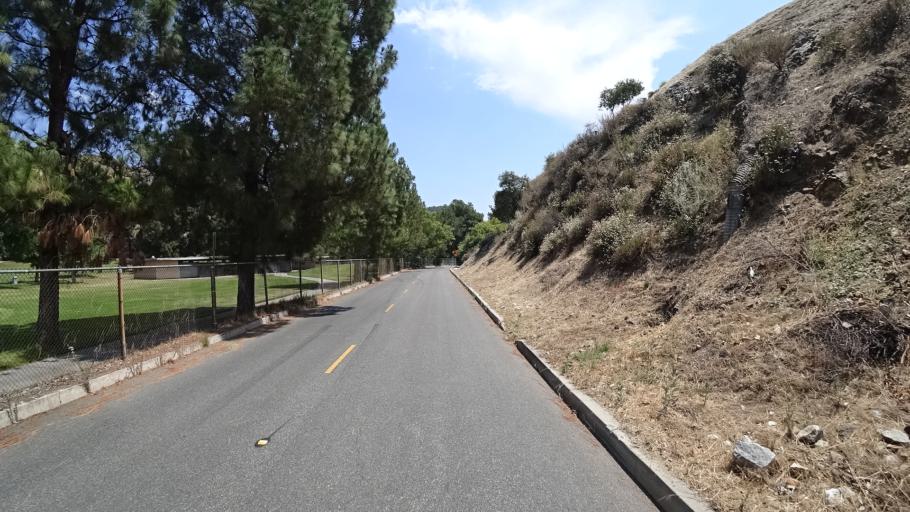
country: US
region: California
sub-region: Los Angeles County
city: Burbank
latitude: 34.2047
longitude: -118.3019
